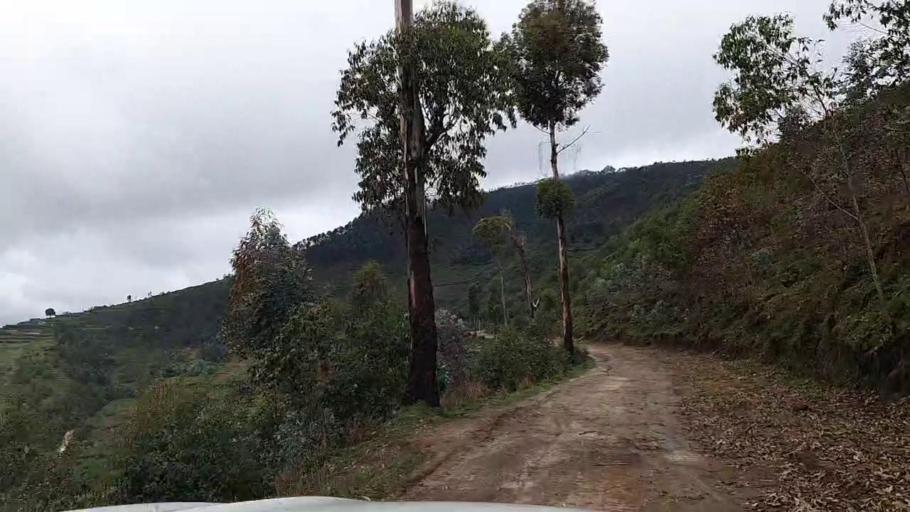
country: RW
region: Southern Province
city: Gikongoro
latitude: -2.3644
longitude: 29.4951
